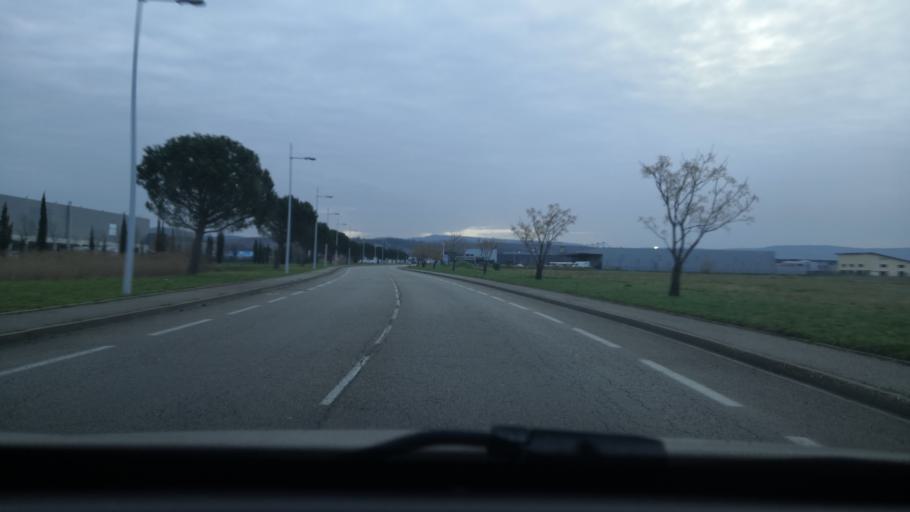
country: FR
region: Rhone-Alpes
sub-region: Departement de la Drome
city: Montelimar
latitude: 44.5272
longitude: 4.7365
